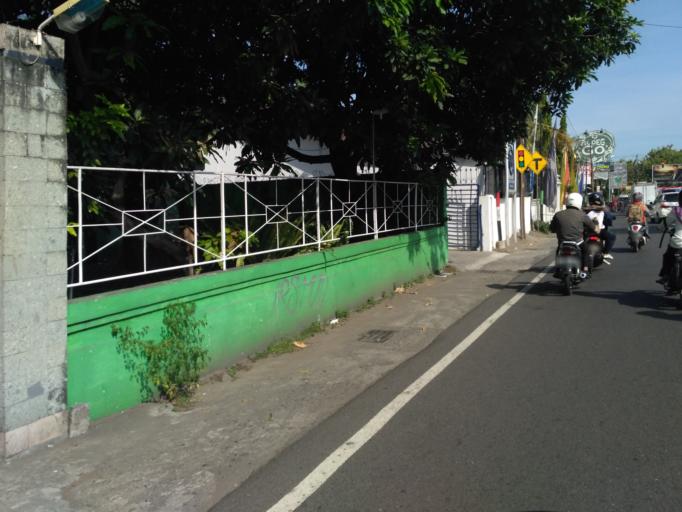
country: ID
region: Daerah Istimewa Yogyakarta
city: Depok
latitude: -7.7821
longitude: 110.4300
